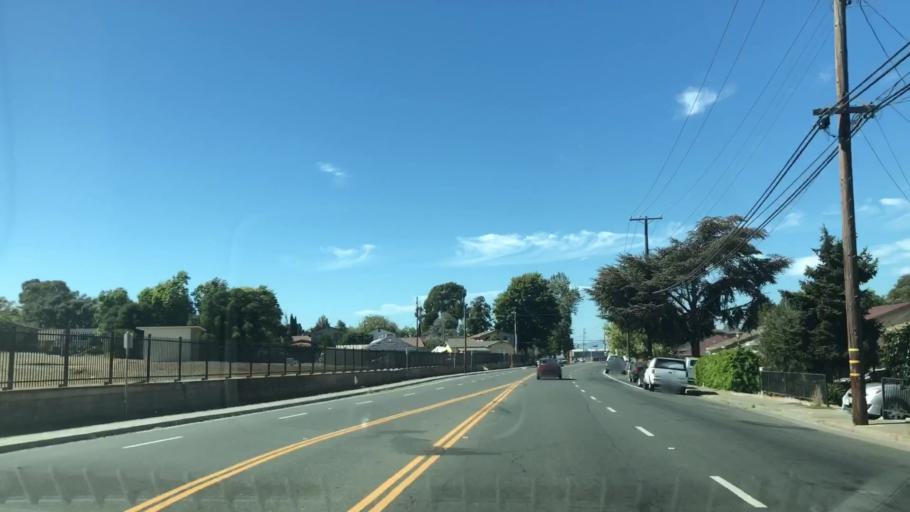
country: US
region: California
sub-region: Solano County
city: Vallejo
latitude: 38.1198
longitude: -122.2603
